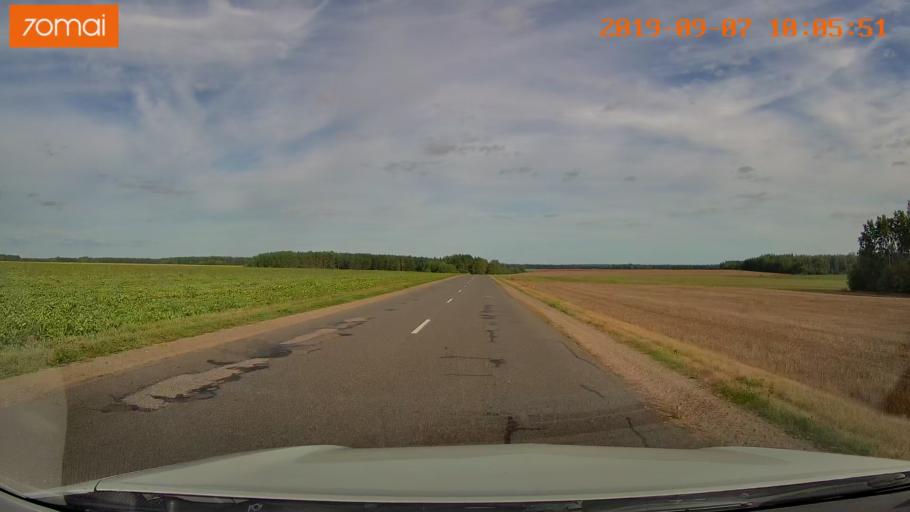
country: BY
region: Grodnenskaya
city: Voranava
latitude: 54.0534
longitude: 25.4051
